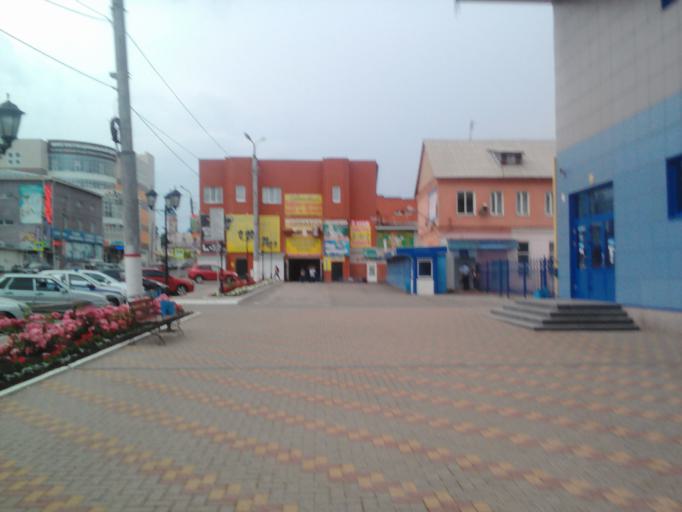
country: RU
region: Kursk
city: Kursk
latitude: 51.7294
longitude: 36.1826
